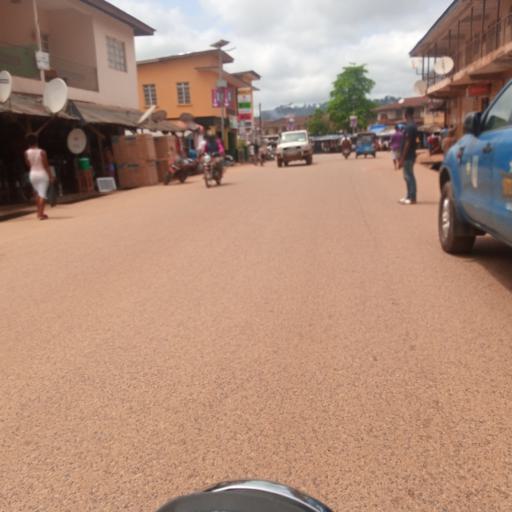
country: SL
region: Eastern Province
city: Kenema
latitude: 7.8768
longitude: -11.1894
